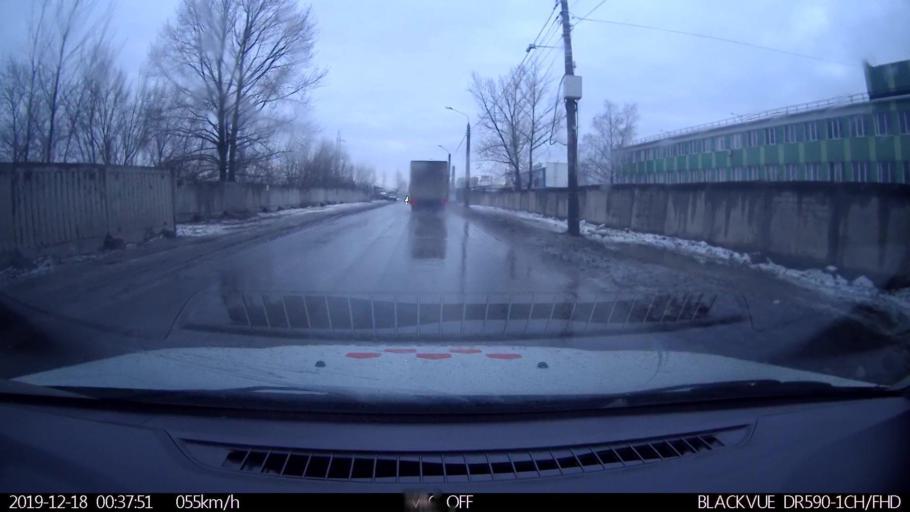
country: RU
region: Nizjnij Novgorod
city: Neklyudovo
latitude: 56.3497
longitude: 43.8933
